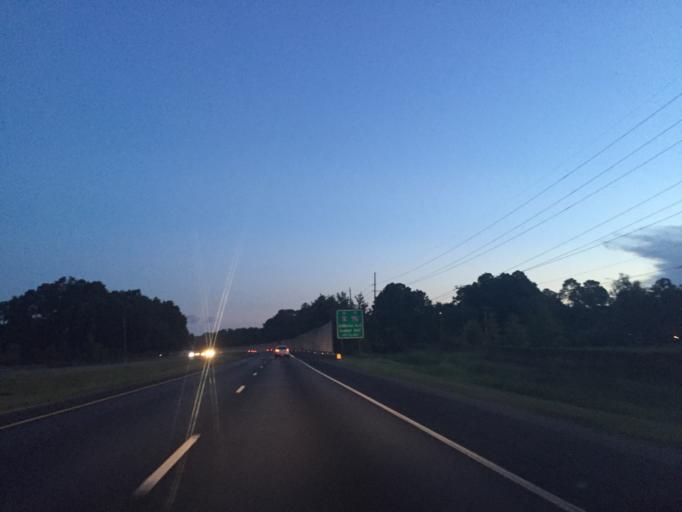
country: US
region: Georgia
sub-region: Chatham County
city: Isle of Hope
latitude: 32.0113
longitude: -81.0823
